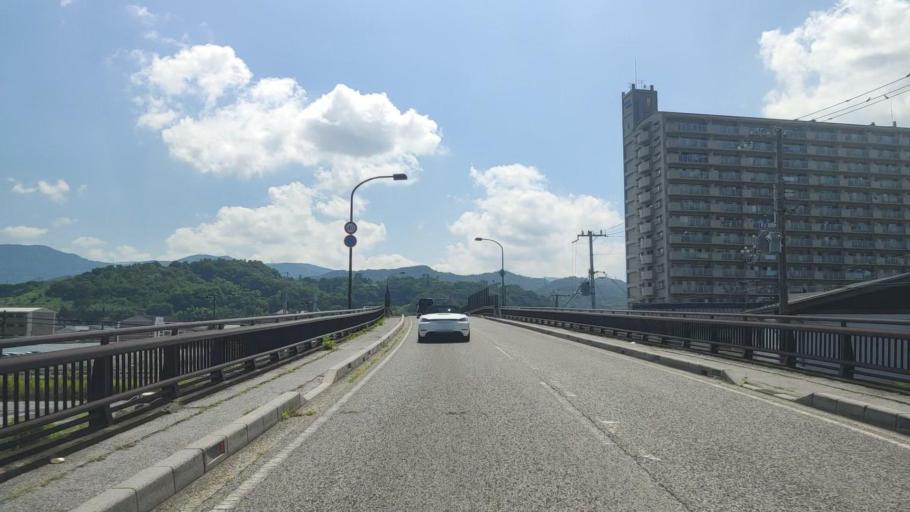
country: JP
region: Shiga Prefecture
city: Hikone
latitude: 35.2683
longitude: 136.2616
